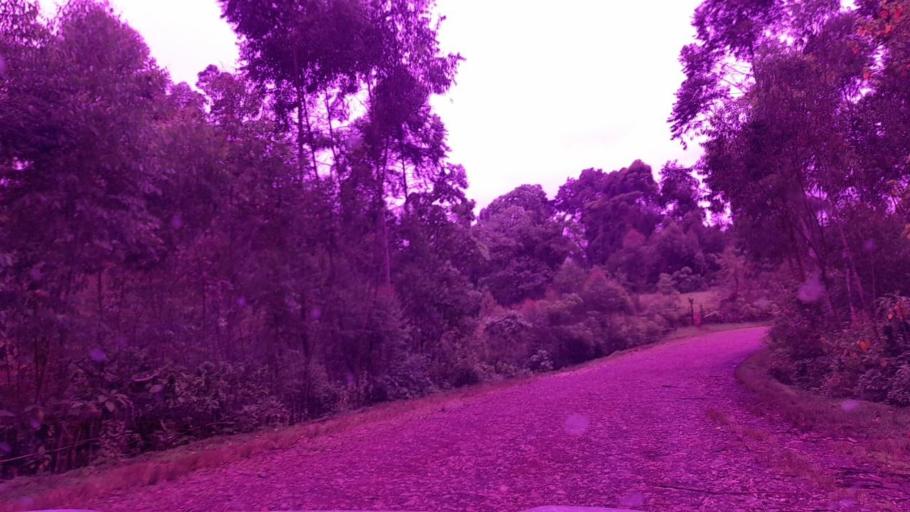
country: ET
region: Southern Nations, Nationalities, and People's Region
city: Tippi
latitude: 7.5868
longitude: 35.7675
